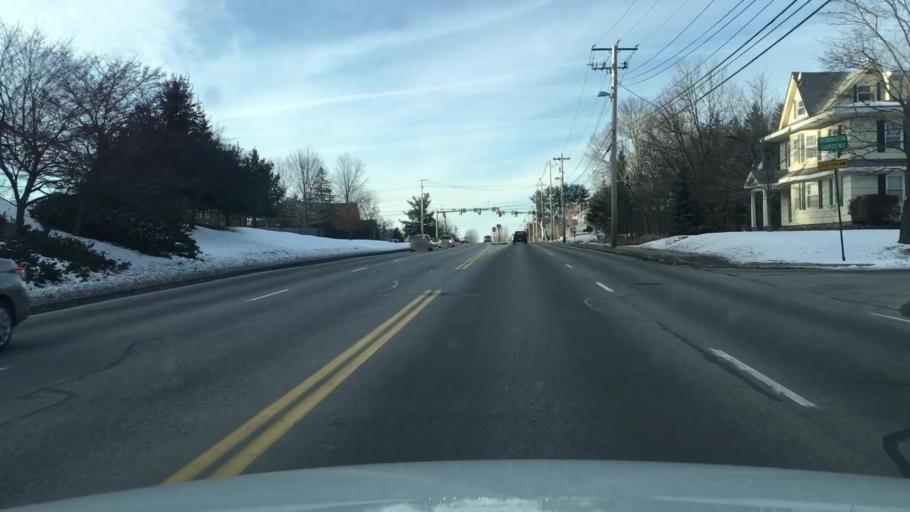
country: US
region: Maine
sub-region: Androscoggin County
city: Lewiston
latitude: 44.1063
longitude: -70.1972
